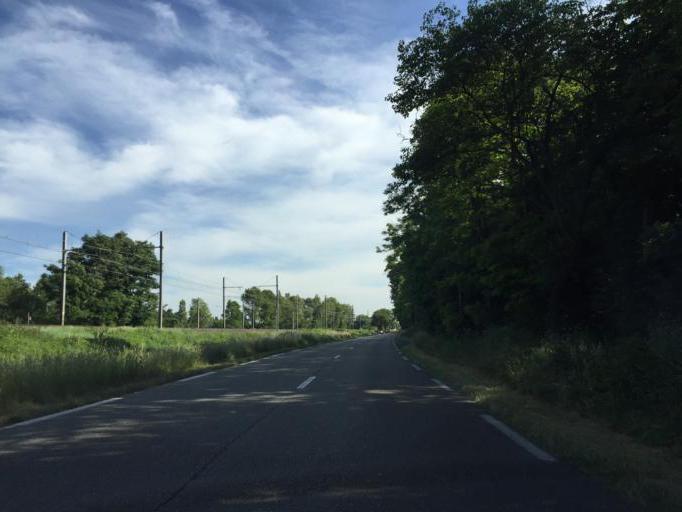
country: FR
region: Rhone-Alpes
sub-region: Departement de l'Ardeche
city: Meysse
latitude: 44.6288
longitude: 4.7430
